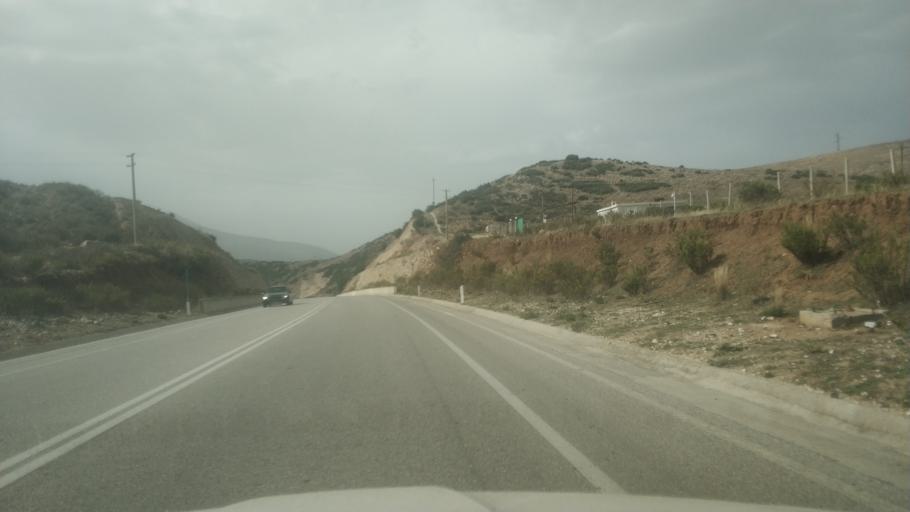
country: AL
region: Gjirokaster
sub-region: Rrethi i Tepelenes
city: Memaliaj
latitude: 40.3639
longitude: 19.9236
